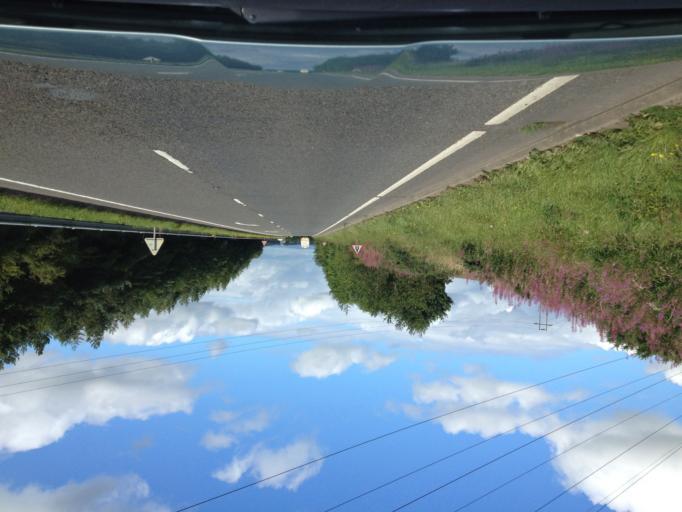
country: GB
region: Scotland
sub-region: West Lothian
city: Armadale
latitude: 55.9028
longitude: -3.6764
